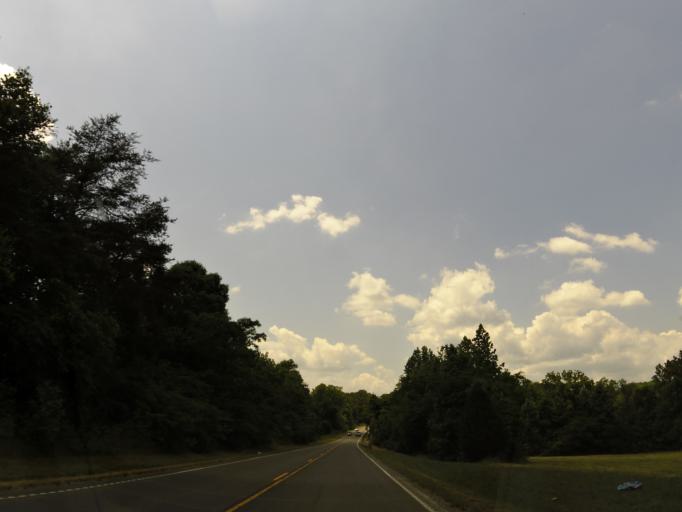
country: US
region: Tennessee
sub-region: Rhea County
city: Spring City
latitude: 35.6465
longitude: -84.8593
